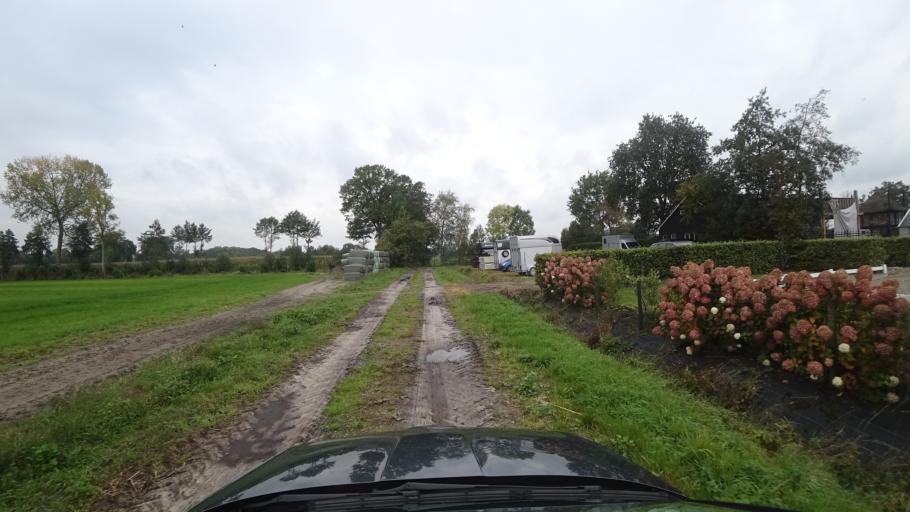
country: NL
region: Gelderland
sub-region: Gemeente Ede
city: Ederveen
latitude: 52.0804
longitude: 5.5920
